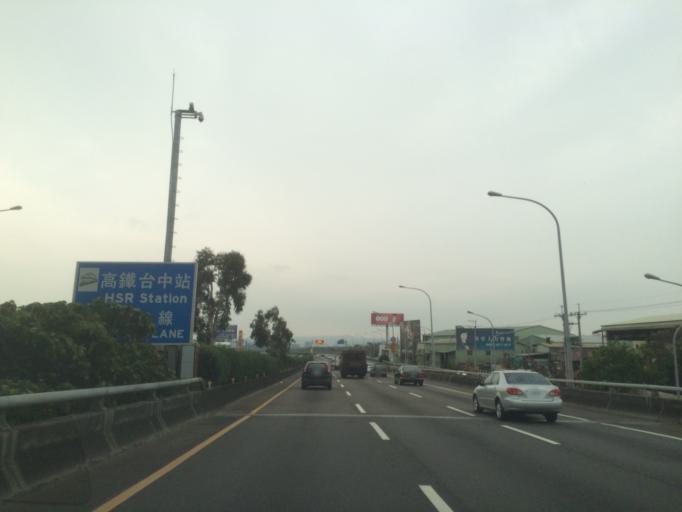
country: TW
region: Taiwan
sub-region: Taichung City
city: Taichung
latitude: 24.1345
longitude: 120.6216
